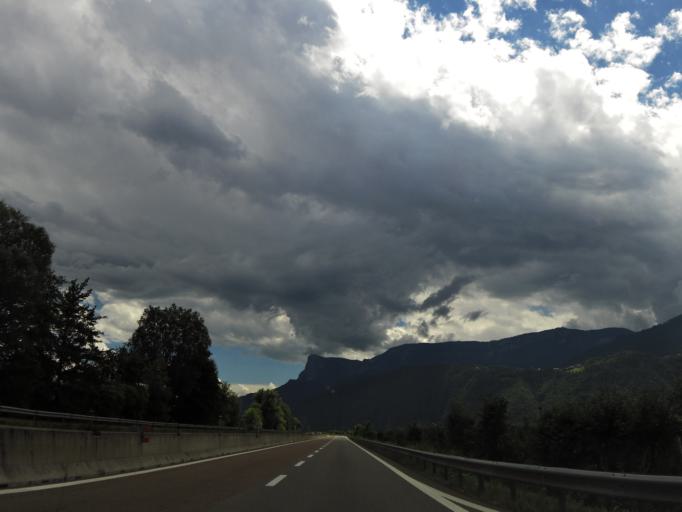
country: IT
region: Trentino-Alto Adige
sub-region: Bolzano
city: Gargazzone
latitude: 46.5914
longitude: 11.1865
